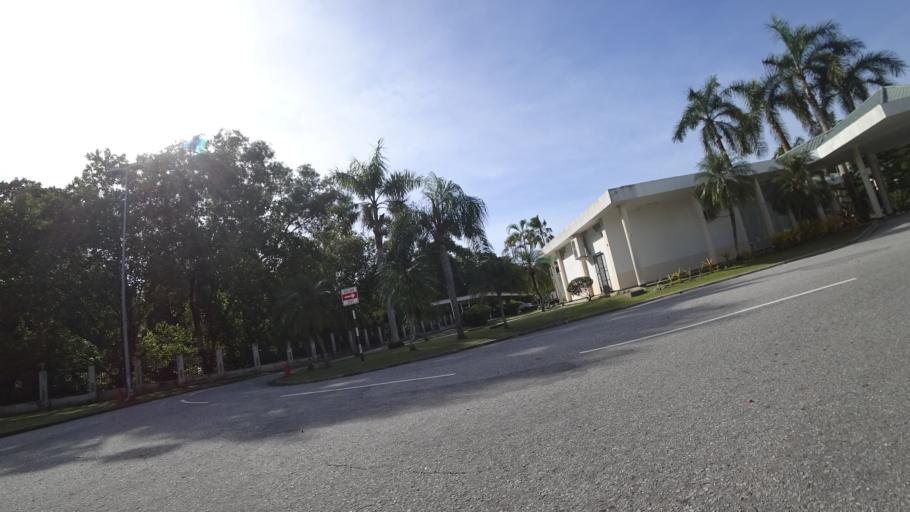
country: BN
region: Brunei and Muara
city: Bandar Seri Begawan
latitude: 4.9354
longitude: 114.8327
